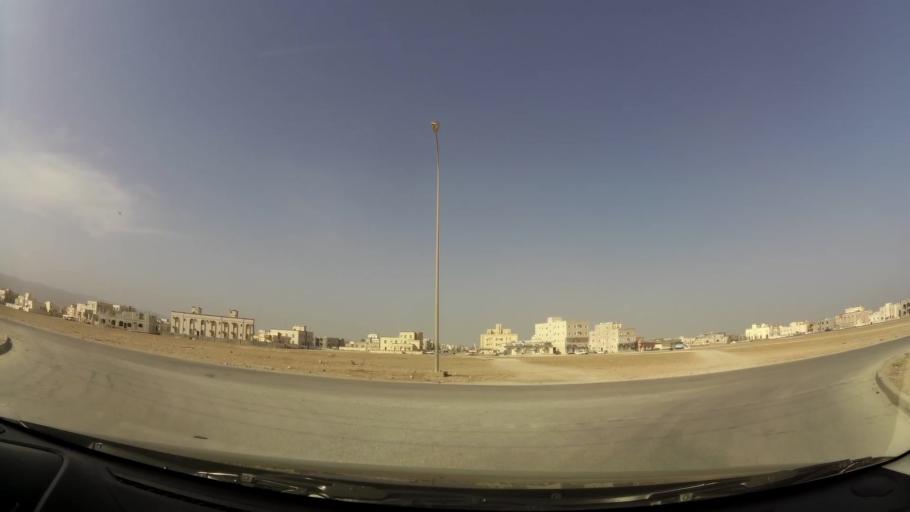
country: OM
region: Zufar
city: Salalah
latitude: 17.0097
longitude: 54.0086
